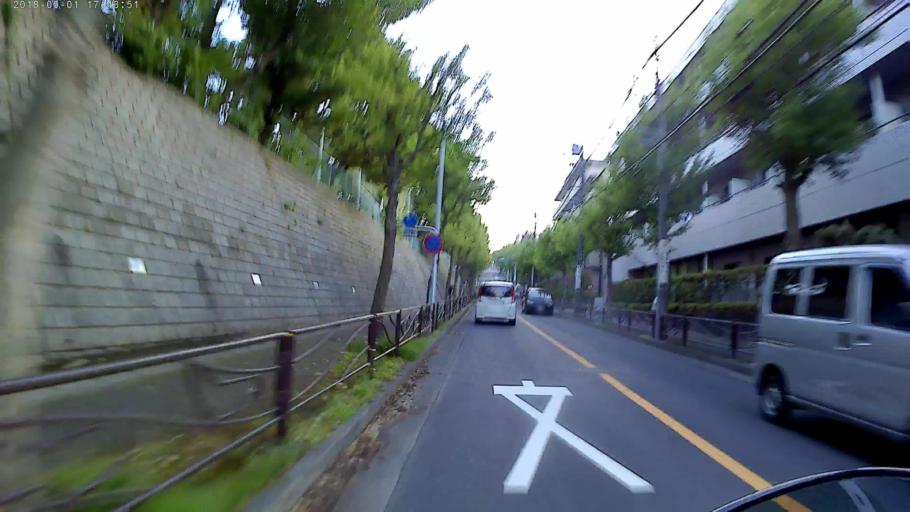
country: JP
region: Tokyo
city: Chofugaoka
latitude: 35.5722
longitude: 139.5764
